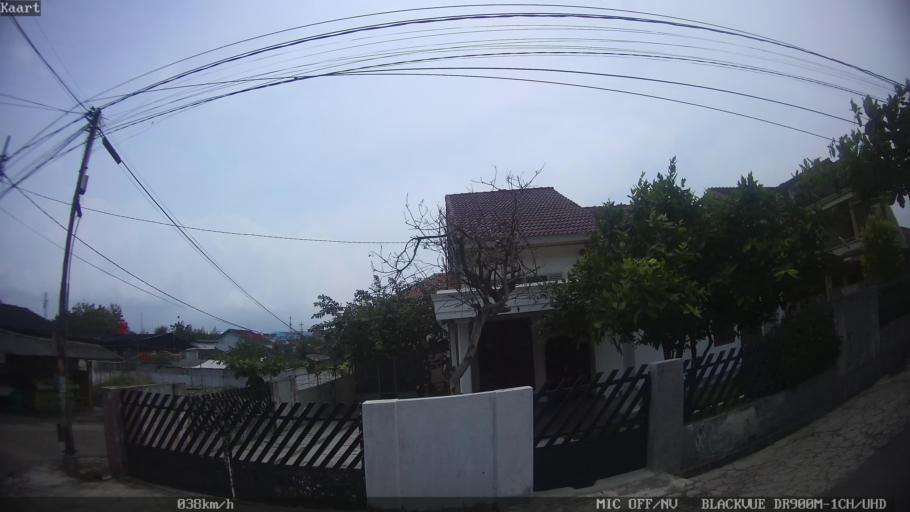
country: ID
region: Lampung
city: Bandarlampung
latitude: -5.4253
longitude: 105.2792
